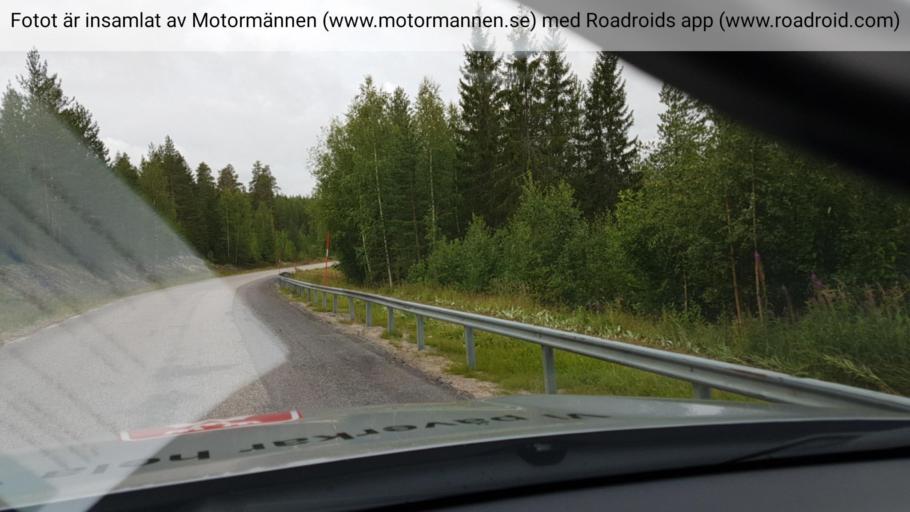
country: SE
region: Norrbotten
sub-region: Bodens Kommun
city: Saevast
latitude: 65.6698
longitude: 21.6934
